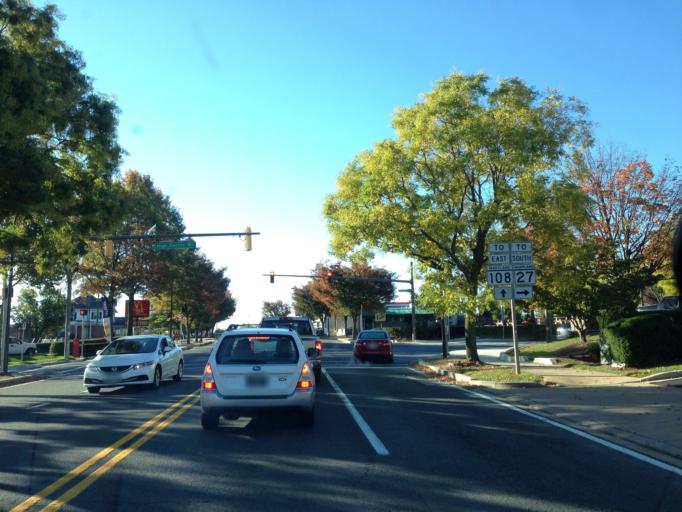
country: US
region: Maryland
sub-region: Montgomery County
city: Damascus
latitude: 39.2907
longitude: -77.2050
